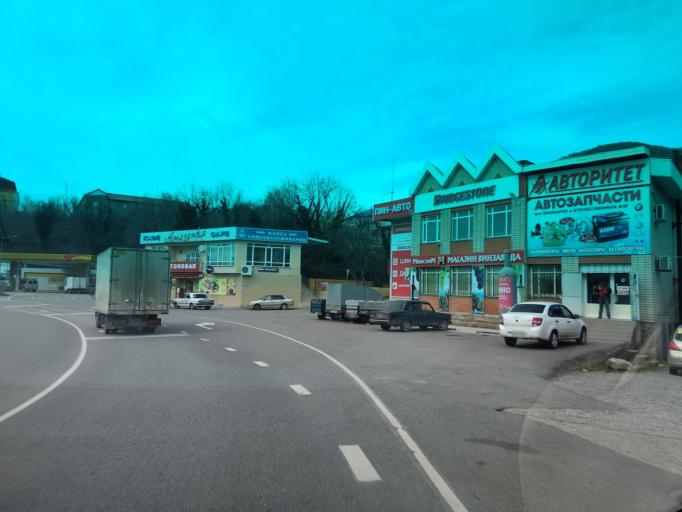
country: RU
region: Krasnodarskiy
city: Tuapse
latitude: 44.0923
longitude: 39.1175
